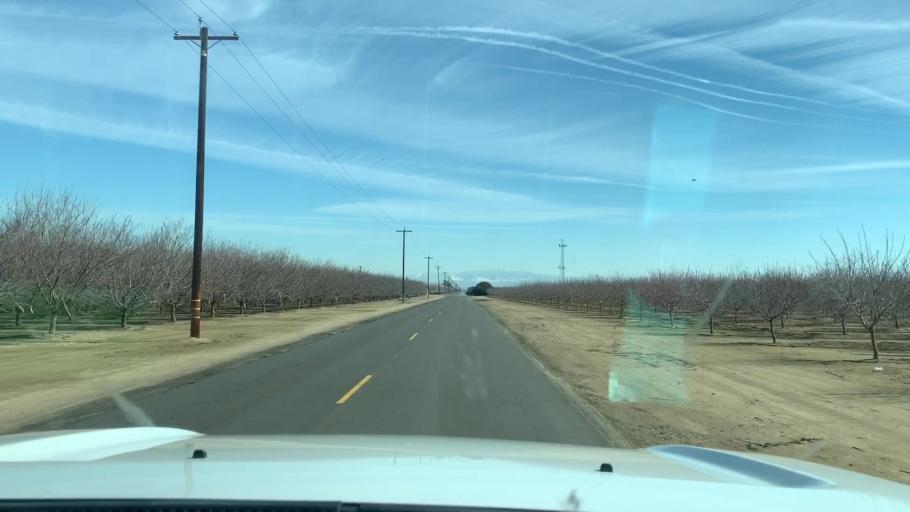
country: US
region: California
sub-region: Kern County
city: Shafter
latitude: 35.4853
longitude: -119.2732
